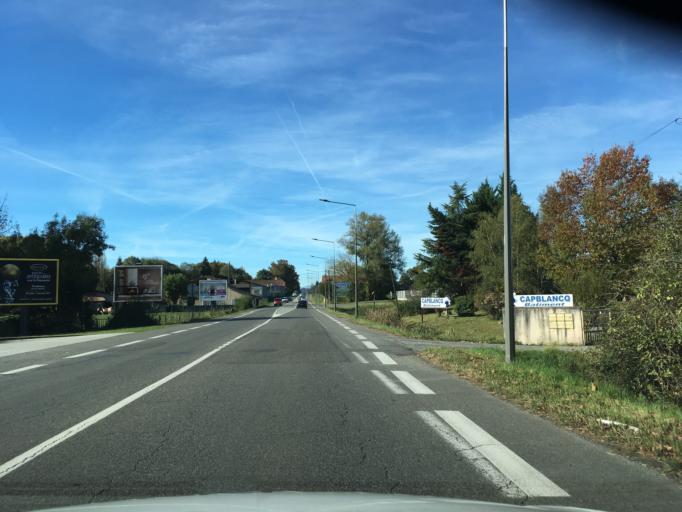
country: FR
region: Aquitaine
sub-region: Departement des Pyrenees-Atlantiques
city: Idron
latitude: 43.3143
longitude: -0.3174
